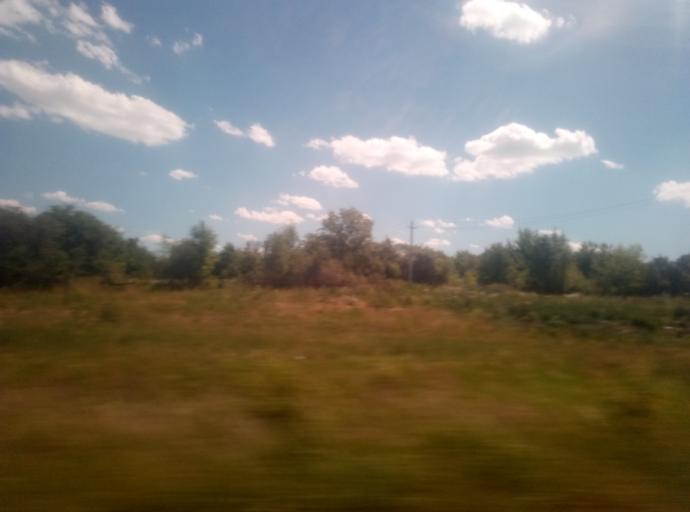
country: RU
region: Tula
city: Kireyevsk
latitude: 53.9375
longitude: 37.9468
